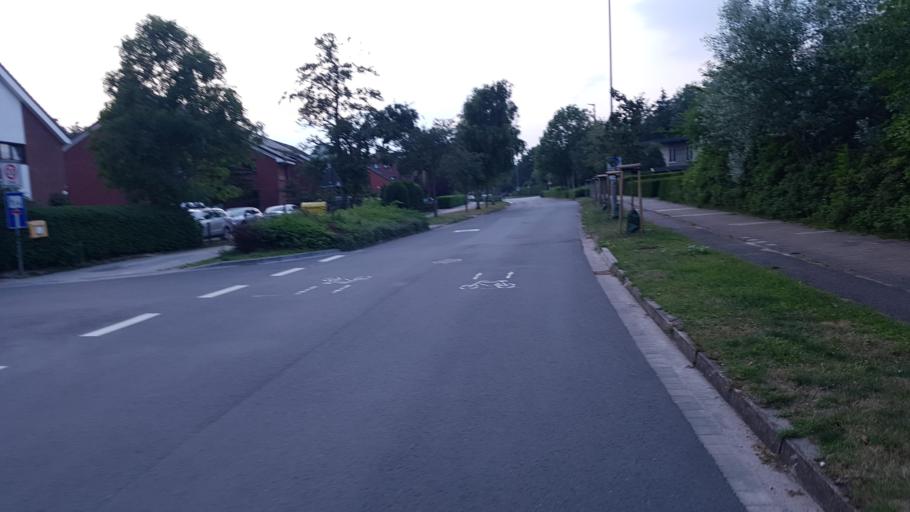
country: DE
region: Schleswig-Holstein
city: Sankt Peter-Ording
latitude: 54.2994
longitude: 8.6427
